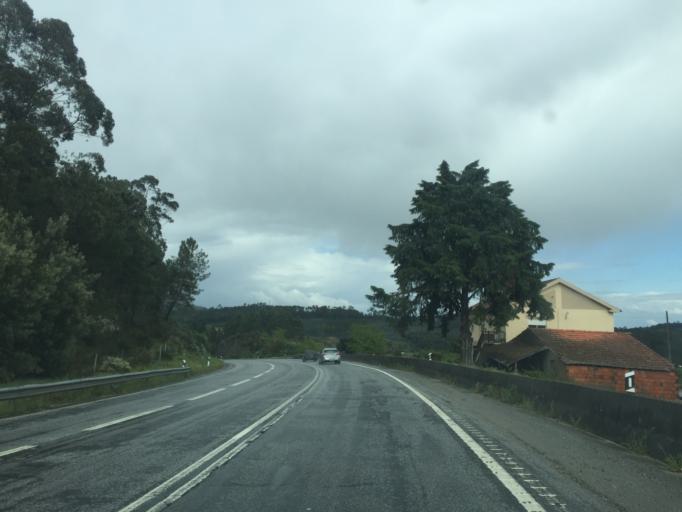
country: PT
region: Viseu
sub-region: Viseu
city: Abraveses
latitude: 40.6602
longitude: -8.0077
